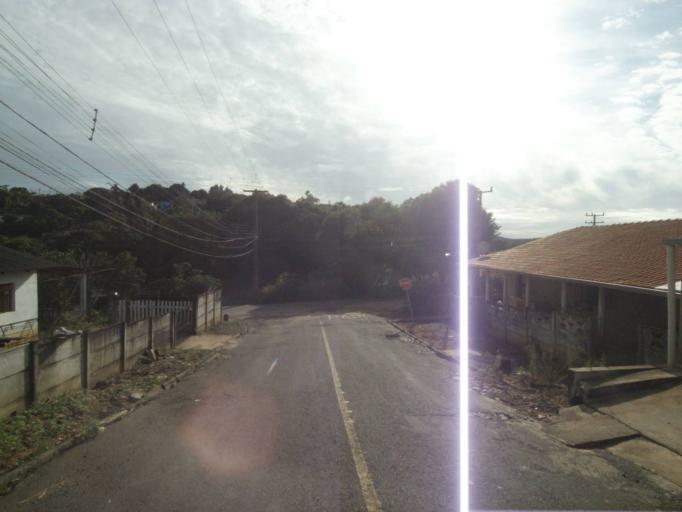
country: BR
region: Parana
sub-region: Telemaco Borba
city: Telemaco Borba
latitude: -24.3414
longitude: -50.6158
